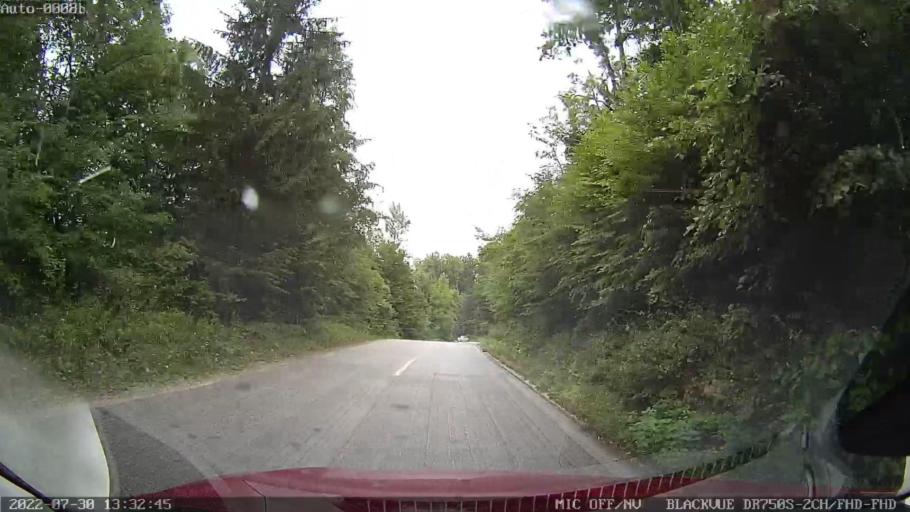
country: SI
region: Zuzemberk
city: Zuzemberk
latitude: 45.8462
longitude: 14.9362
